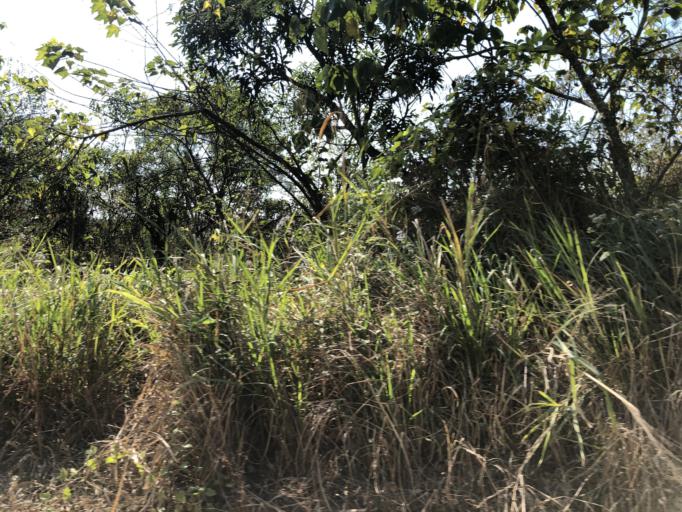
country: TW
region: Taiwan
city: Yujing
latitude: 23.0482
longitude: 120.3701
